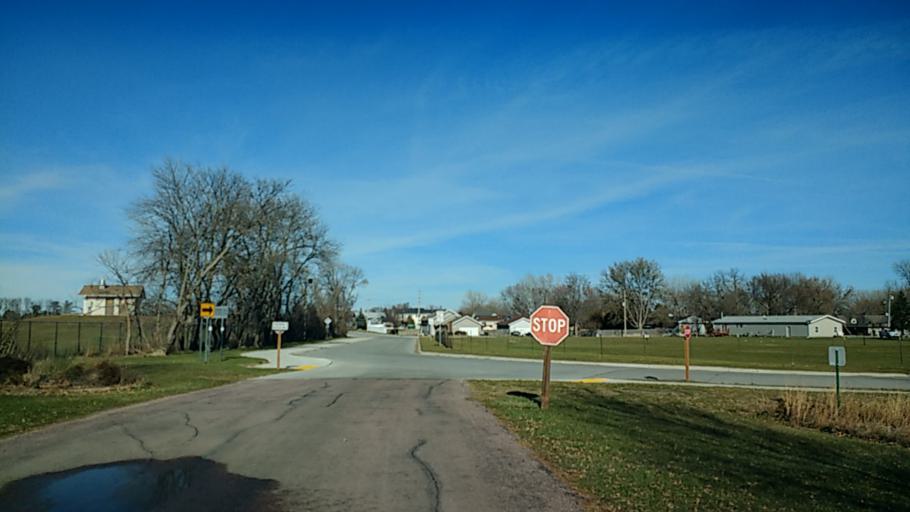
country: US
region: South Dakota
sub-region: Union County
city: North Sioux City
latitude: 42.5404
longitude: -96.5270
